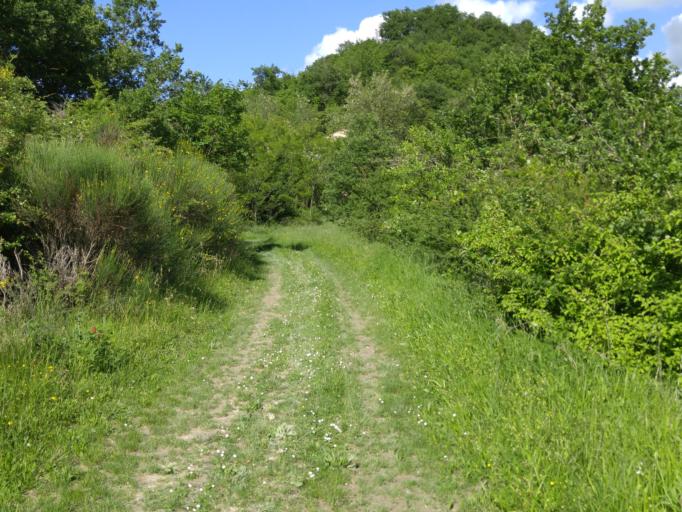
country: IT
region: The Marches
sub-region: Provincia di Pesaro e Urbino
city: Fermignano
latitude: 43.6957
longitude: 12.6312
